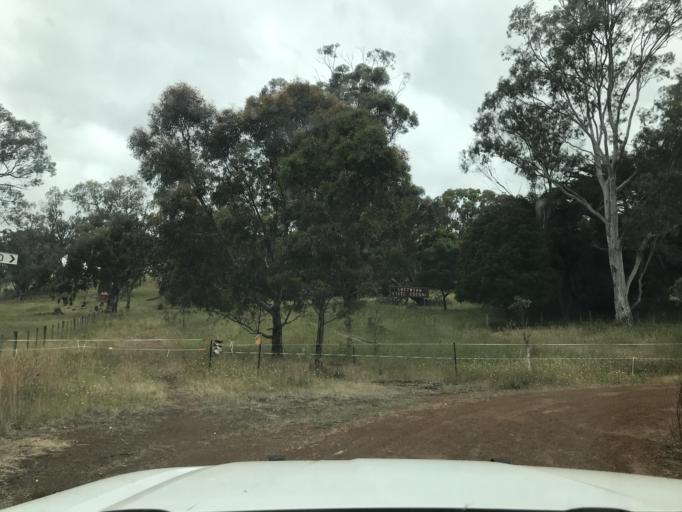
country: AU
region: South Australia
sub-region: Wattle Range
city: Penola
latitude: -37.2783
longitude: 141.4208
